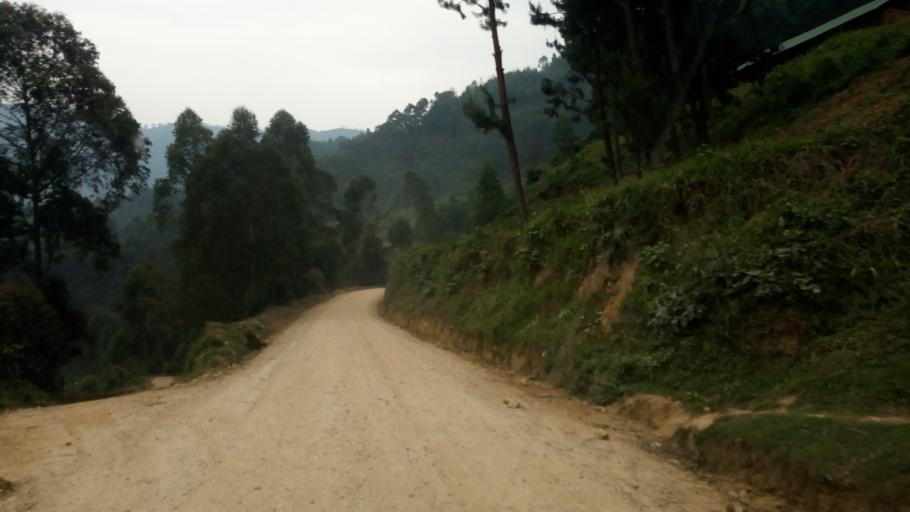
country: UG
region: Western Region
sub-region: Kanungu District
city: Kanungu
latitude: -1.0993
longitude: 29.8518
